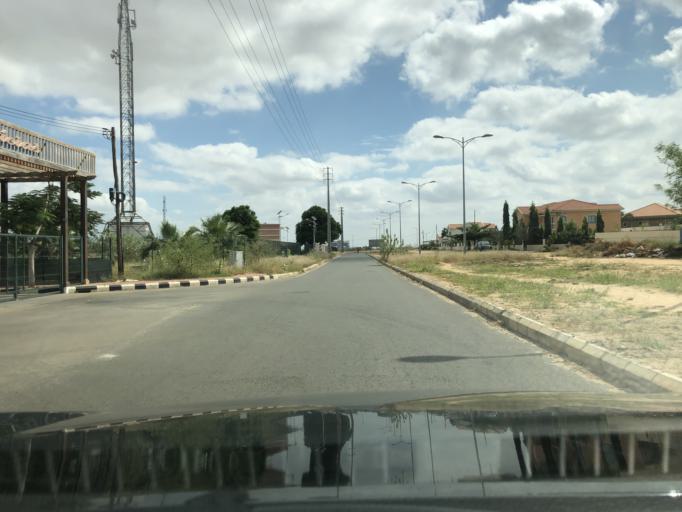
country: AO
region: Luanda
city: Luanda
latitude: -8.9698
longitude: 13.2414
